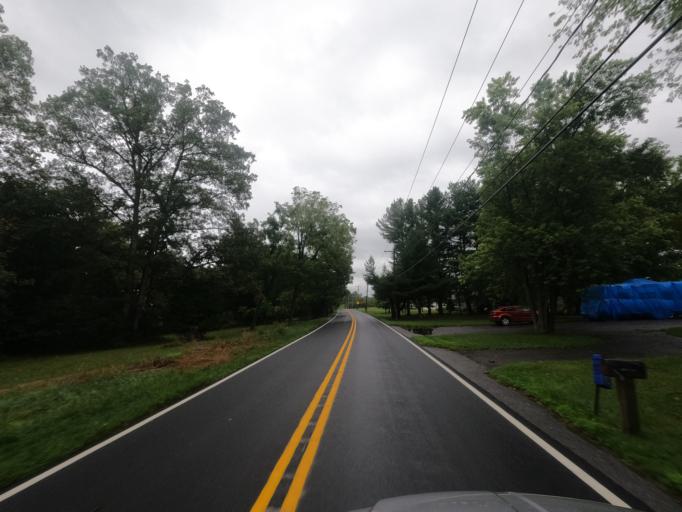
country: US
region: West Virginia
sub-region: Berkeley County
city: Martinsburg
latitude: 39.6178
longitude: -77.9966
